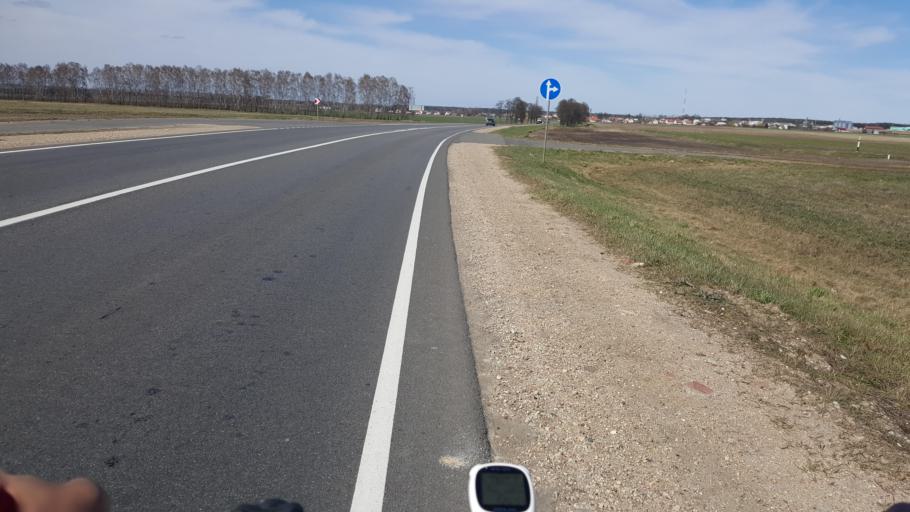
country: BY
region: Brest
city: Kamyanyets
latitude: 52.3110
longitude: 23.7807
